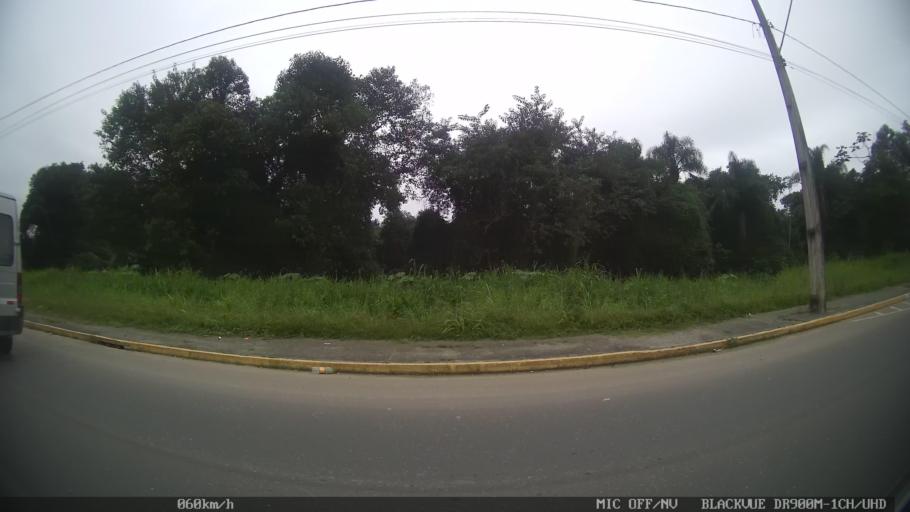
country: BR
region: Santa Catarina
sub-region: Joinville
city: Joinville
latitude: -26.2908
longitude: -48.8921
